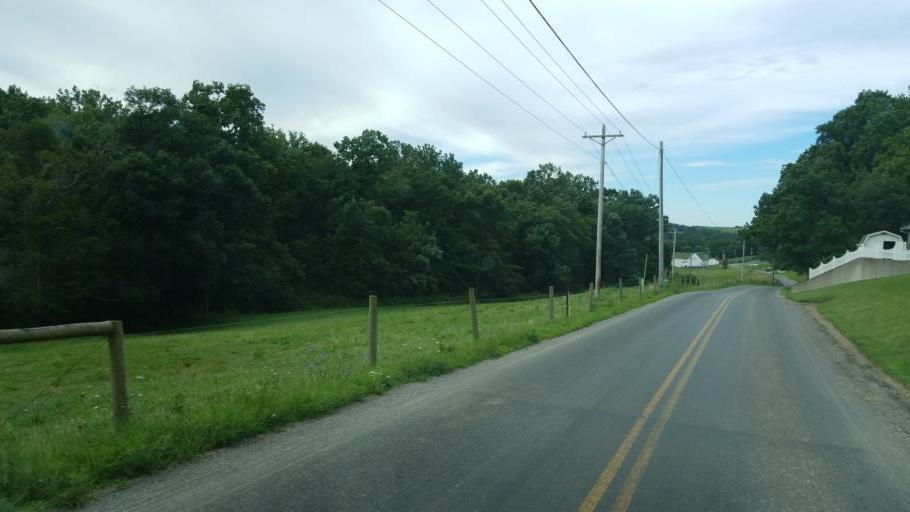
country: US
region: Ohio
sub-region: Holmes County
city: Millersburg
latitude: 40.4982
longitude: -81.8022
